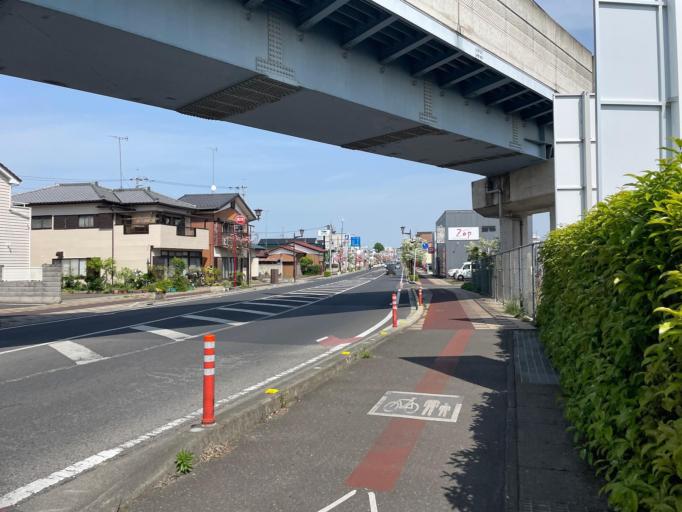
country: JP
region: Gunma
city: Ota
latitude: 36.2961
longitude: 139.3642
